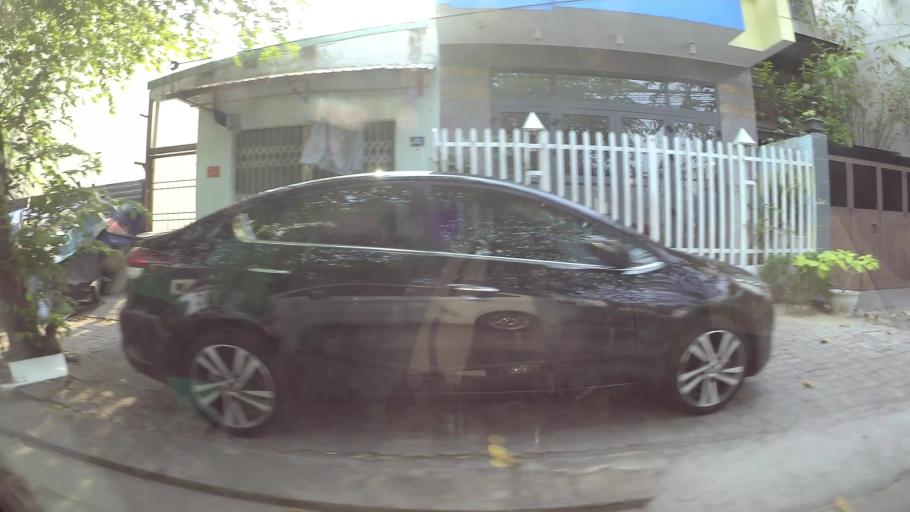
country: VN
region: Da Nang
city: Son Tra
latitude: 16.0424
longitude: 108.2139
